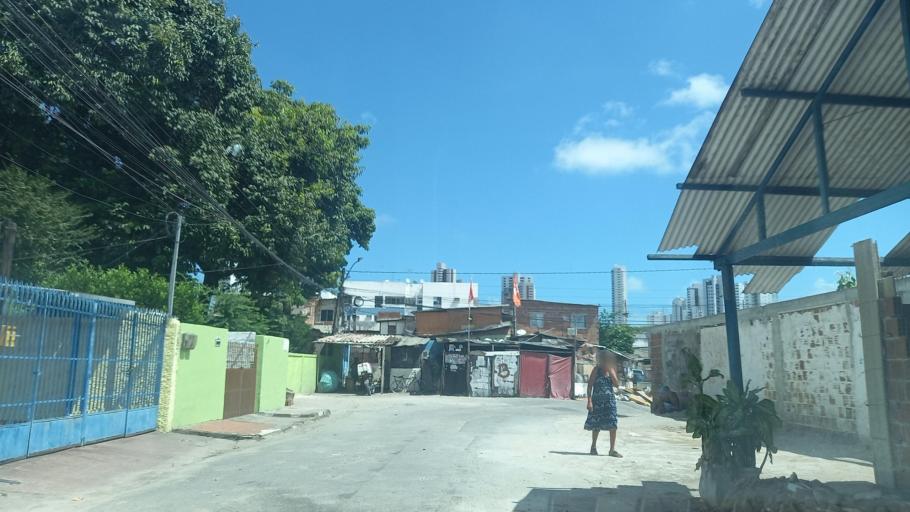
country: BR
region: Pernambuco
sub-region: Recife
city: Recife
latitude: -8.0277
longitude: -34.9018
